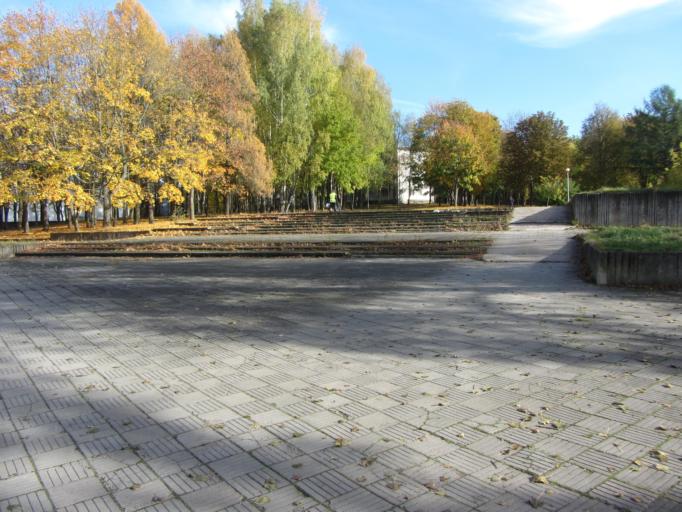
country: LT
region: Vilnius County
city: Elektrenai
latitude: 54.7814
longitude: 24.6594
